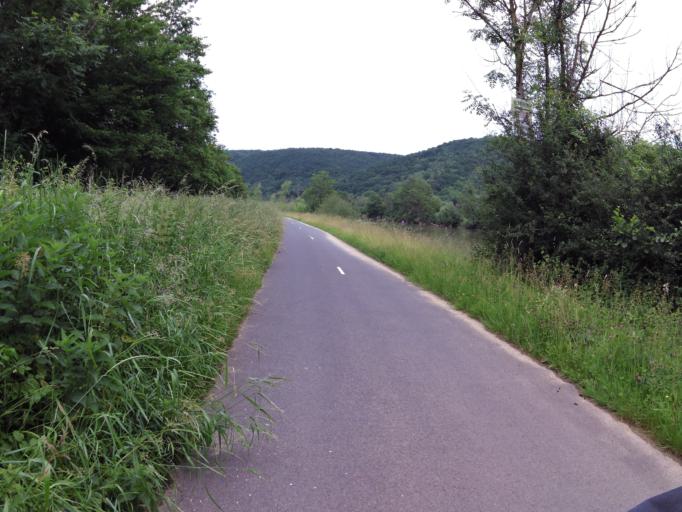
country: FR
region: Champagne-Ardenne
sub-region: Departement des Ardennes
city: Aiglemont
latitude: 49.7923
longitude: 4.7576
